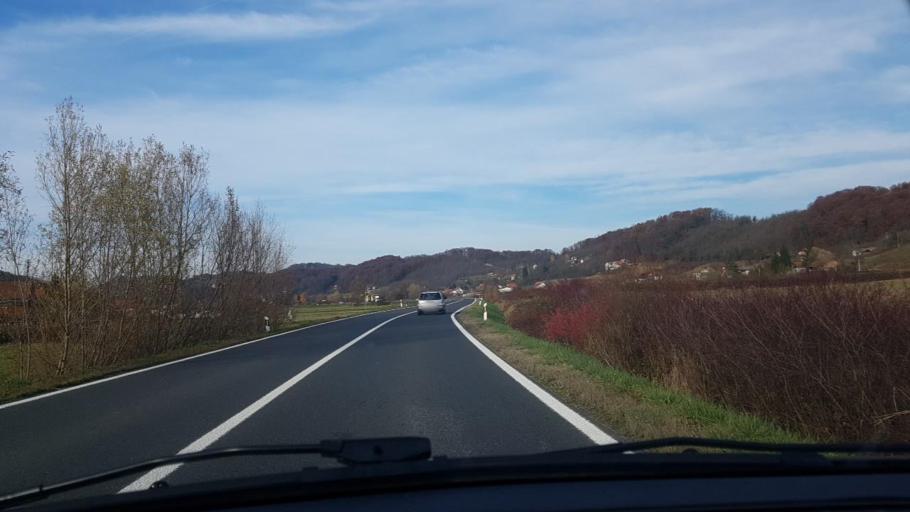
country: HR
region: Krapinsko-Zagorska
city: Zabok
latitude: 46.0668
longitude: 15.8570
